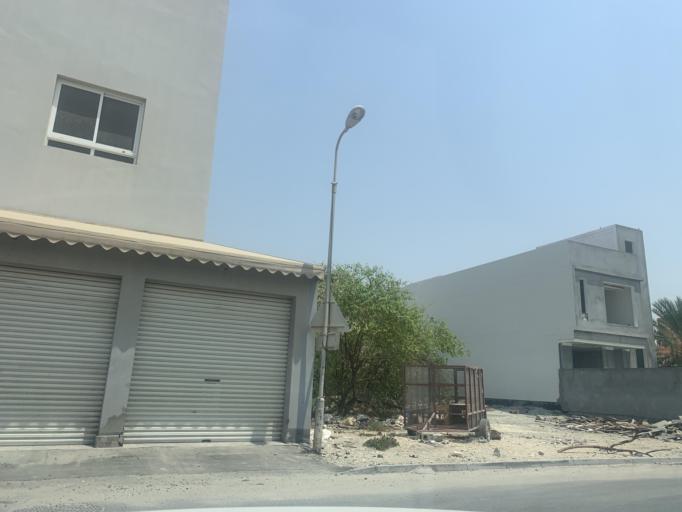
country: BH
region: Central Governorate
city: Madinat Hamad
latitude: 26.1434
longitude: 50.4629
